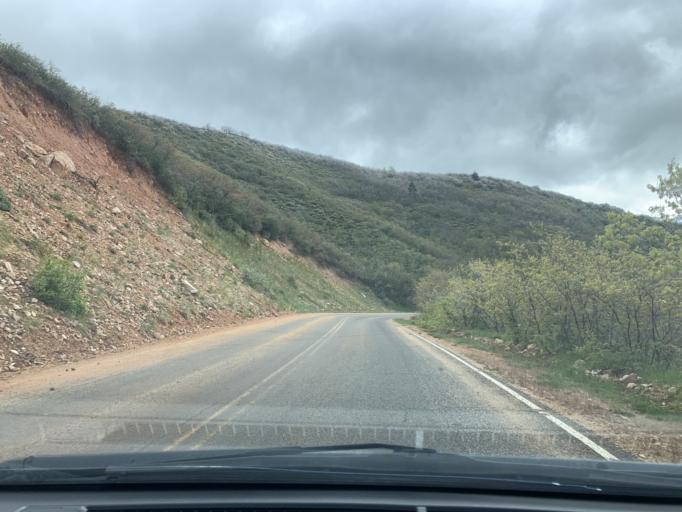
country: US
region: Utah
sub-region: Sanpete County
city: Fountain Green
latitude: 39.7880
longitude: -111.6844
